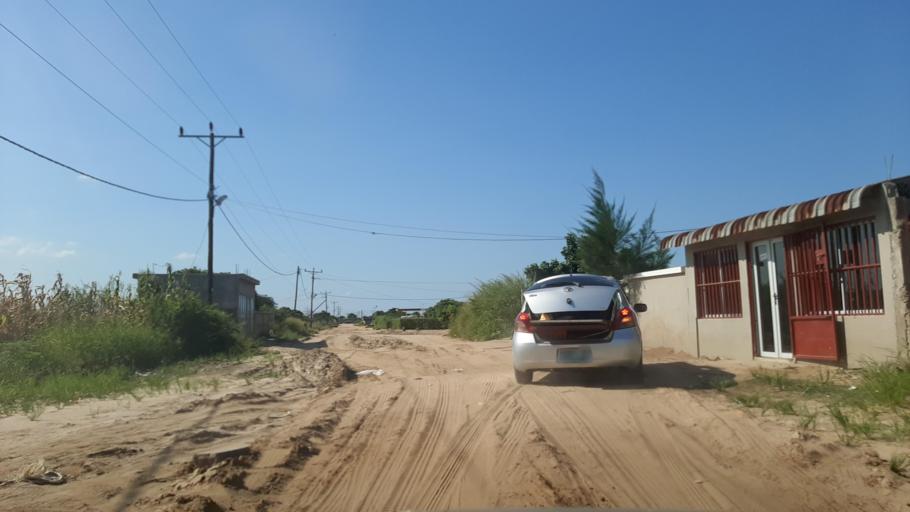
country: MZ
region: Maputo
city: Matola
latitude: -25.8144
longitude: 32.4916
